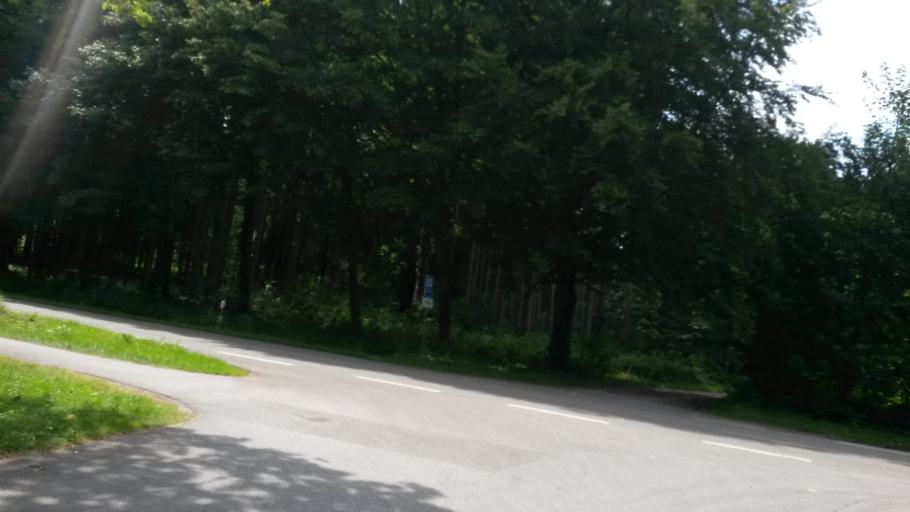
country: DE
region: Bavaria
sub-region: Upper Bavaria
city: Gstadt am Chiemsee
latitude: 47.8948
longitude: 12.4252
